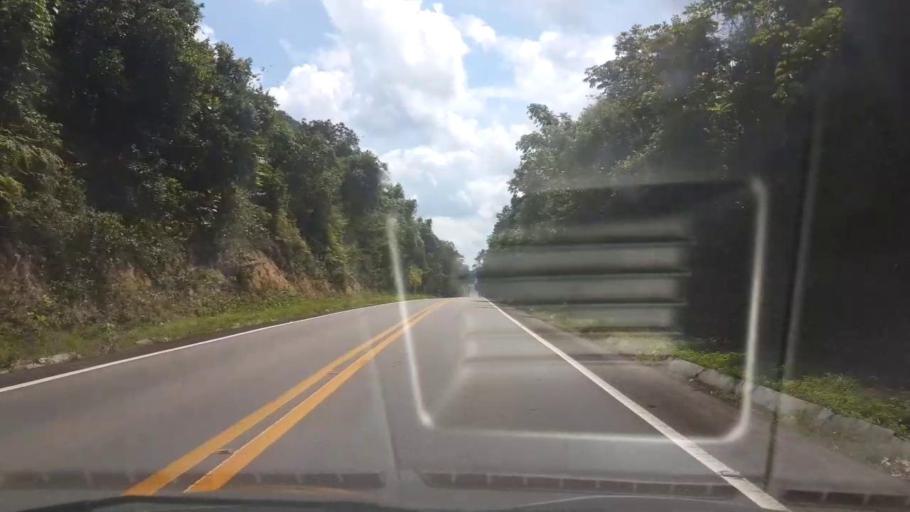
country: BR
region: Amazonas
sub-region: Rio Preto Da Eva
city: Rio Preto da Eva
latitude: -2.4966
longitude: -60.0350
